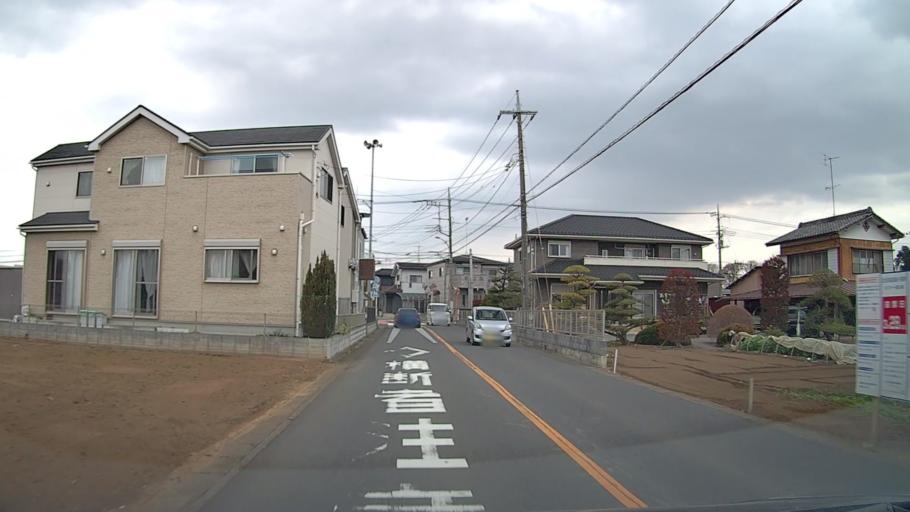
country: JP
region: Saitama
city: Shiki
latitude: 35.8434
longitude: 139.5670
